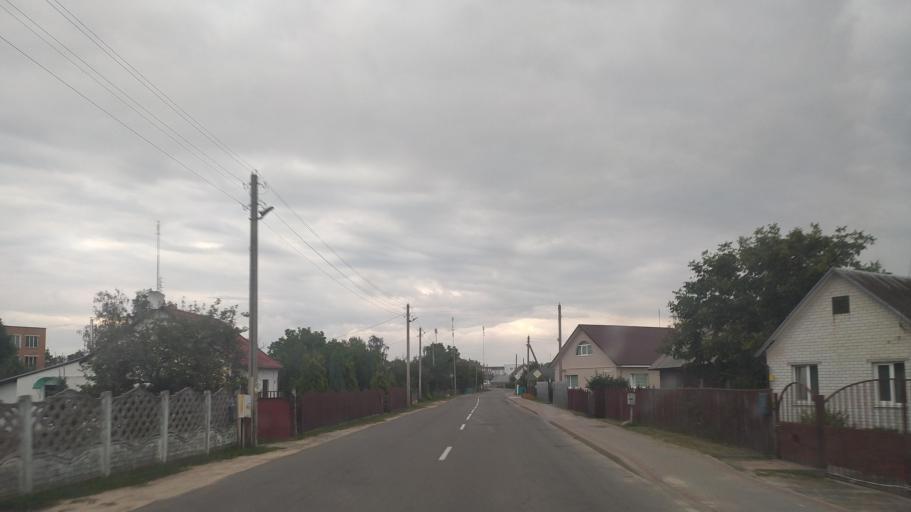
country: BY
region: Brest
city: Byaroza
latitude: 52.5254
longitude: 24.9743
